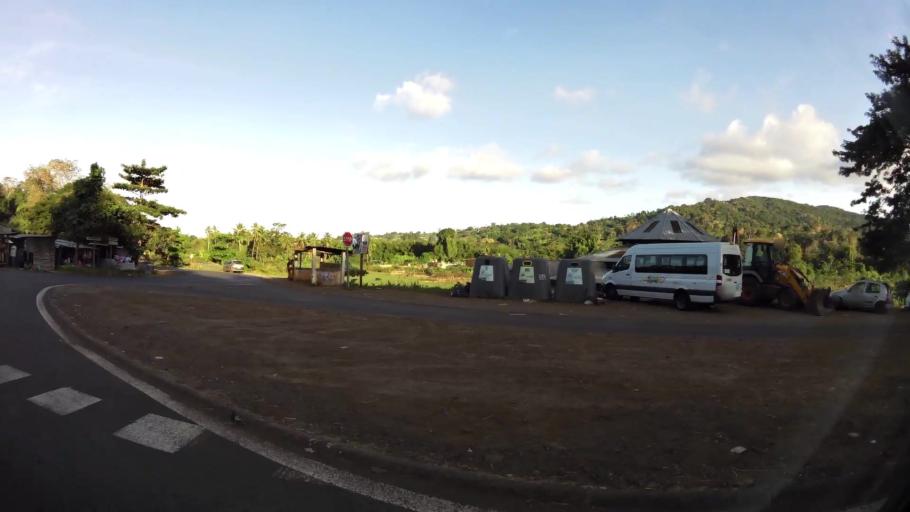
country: YT
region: Dembeni
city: Dembeni
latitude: -12.8367
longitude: 45.1771
